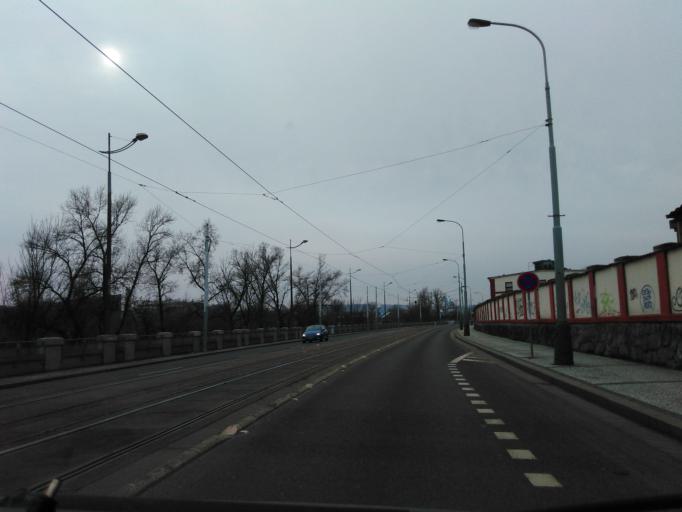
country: CZ
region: Praha
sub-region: Praha 8
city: Karlin
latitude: 50.0987
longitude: 14.4492
